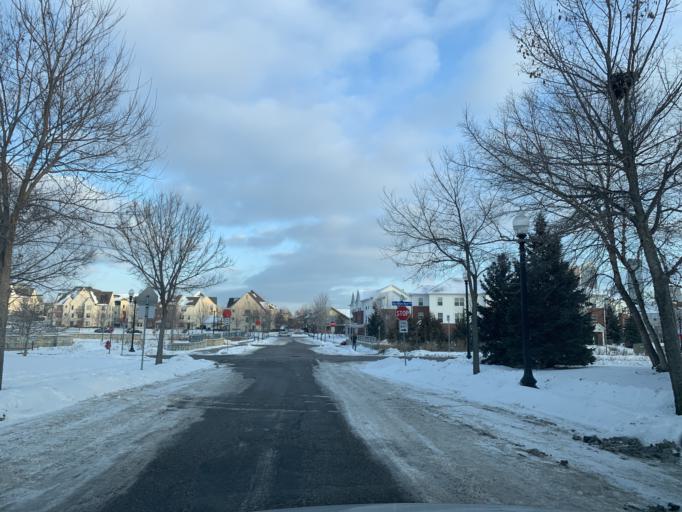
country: US
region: Minnesota
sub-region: Hennepin County
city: Minneapolis
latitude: 44.9864
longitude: -93.2932
